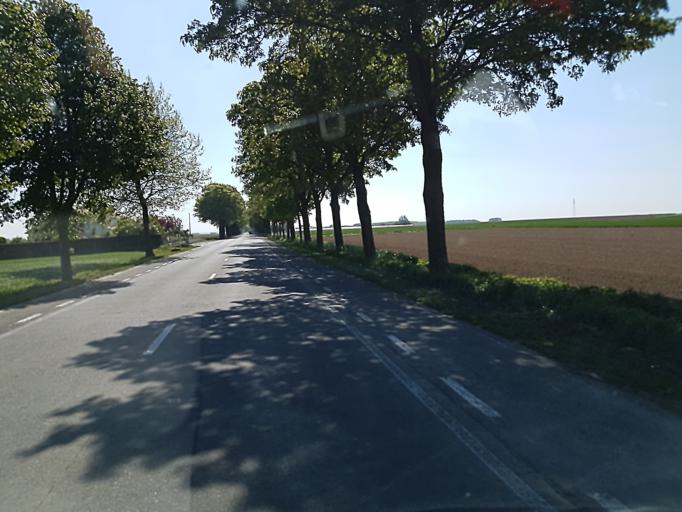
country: BE
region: Wallonia
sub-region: Province du Hainaut
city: Lens
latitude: 50.5676
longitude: 3.8823
